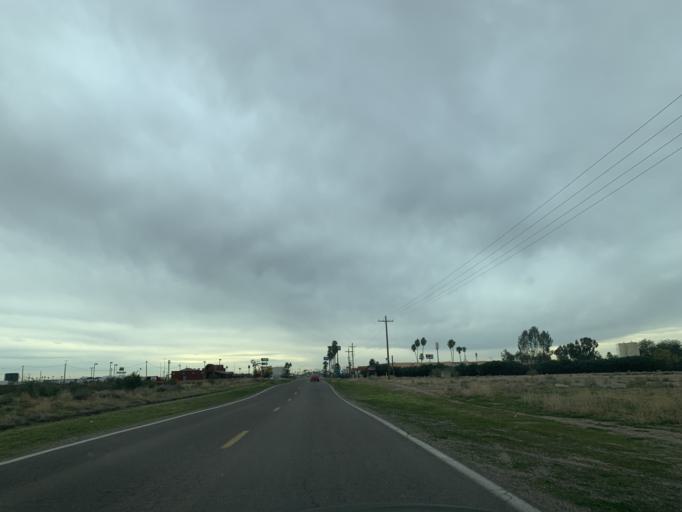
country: US
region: Arizona
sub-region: Pinal County
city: Arizona City
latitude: 32.8170
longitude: -111.6711
